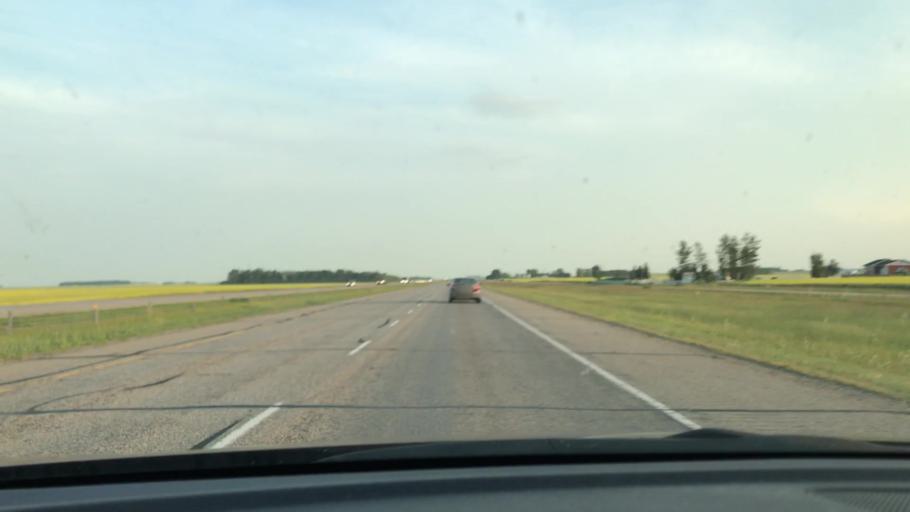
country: CA
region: Alberta
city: Olds
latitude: 51.8448
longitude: -114.0256
